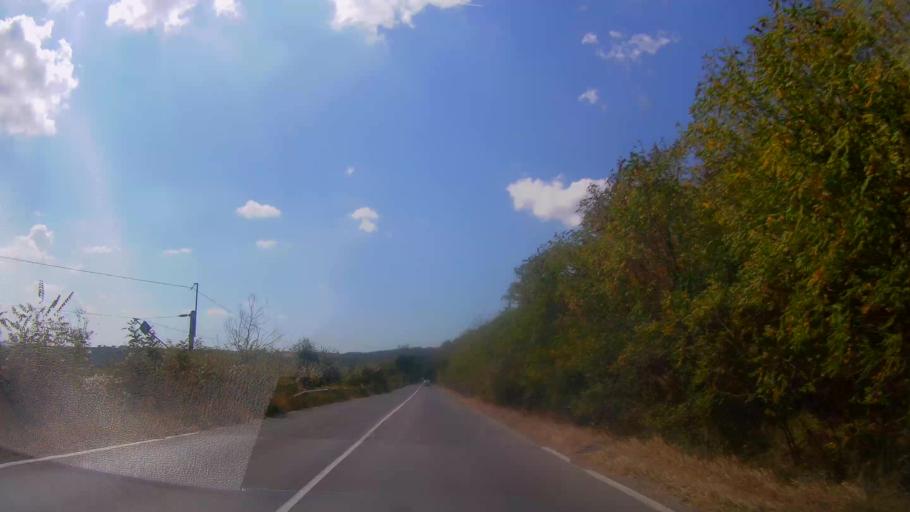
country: BG
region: Veliko Turnovo
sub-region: Obshtina Polski Trumbesh
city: Polski Trumbesh
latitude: 43.4454
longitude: 25.6568
